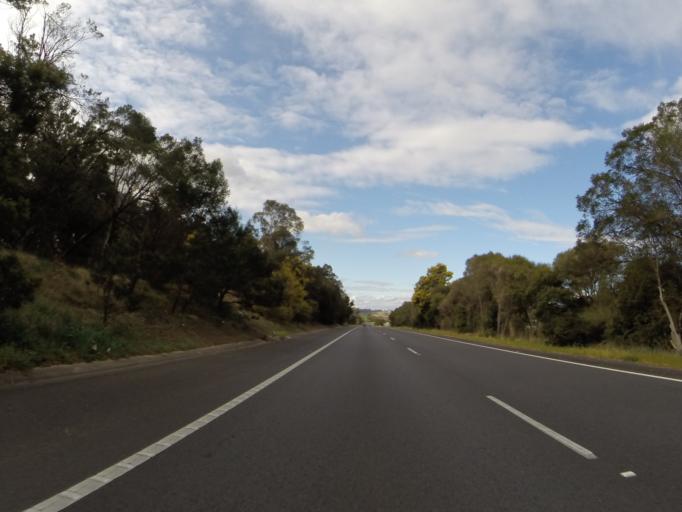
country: AU
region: New South Wales
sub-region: Wingecarribee
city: Bundanoon
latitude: -34.5989
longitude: 150.2375
